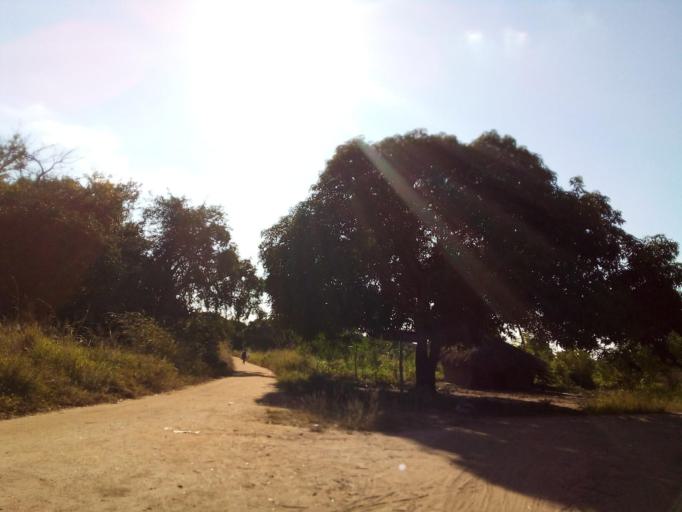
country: MZ
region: Zambezia
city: Quelimane
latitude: -17.5301
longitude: 36.6828
